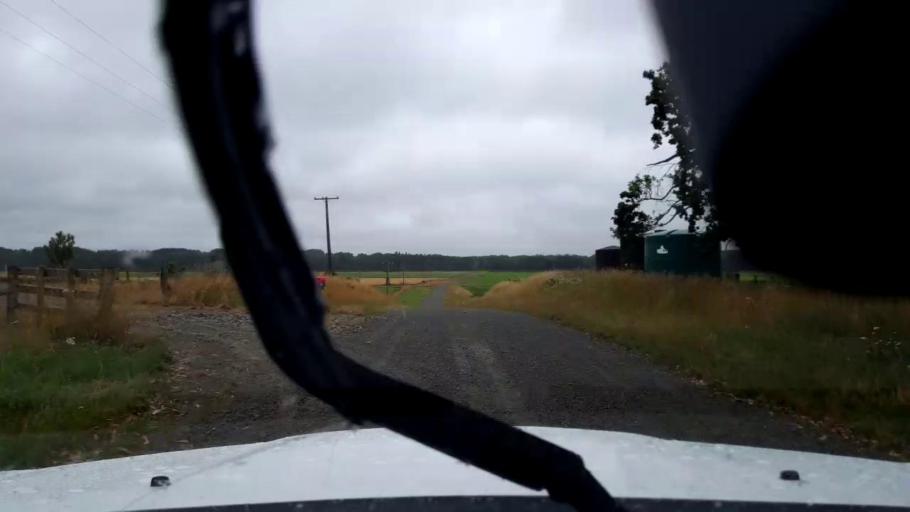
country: NZ
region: Canterbury
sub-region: Timaru District
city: Pleasant Point
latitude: -44.2509
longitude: 171.2004
